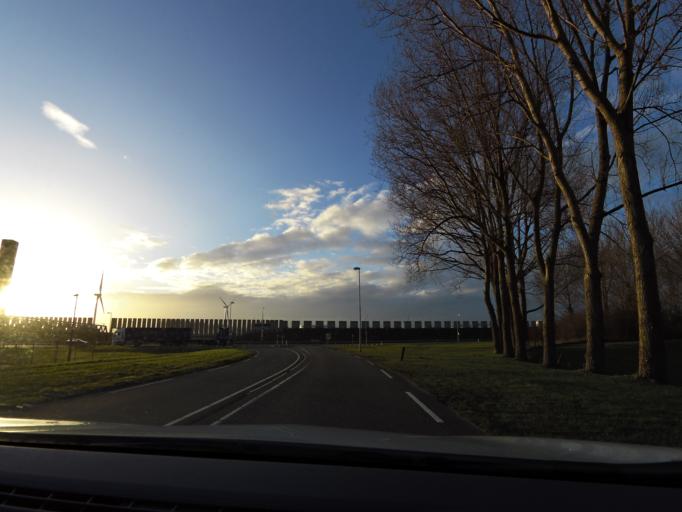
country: NL
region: South Holland
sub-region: Gemeente Maassluis
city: Maassluis
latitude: 51.9032
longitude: 4.2298
